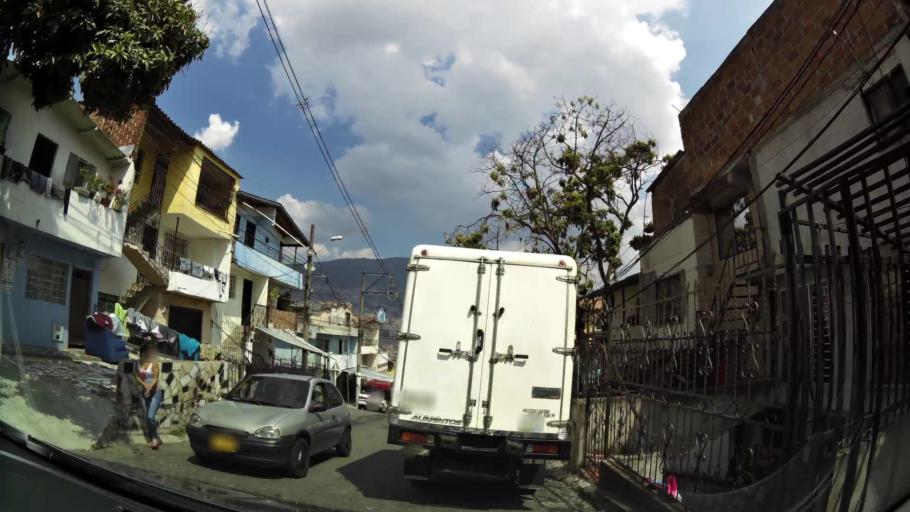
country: CO
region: Antioquia
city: Medellin
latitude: 6.2900
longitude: -75.5768
